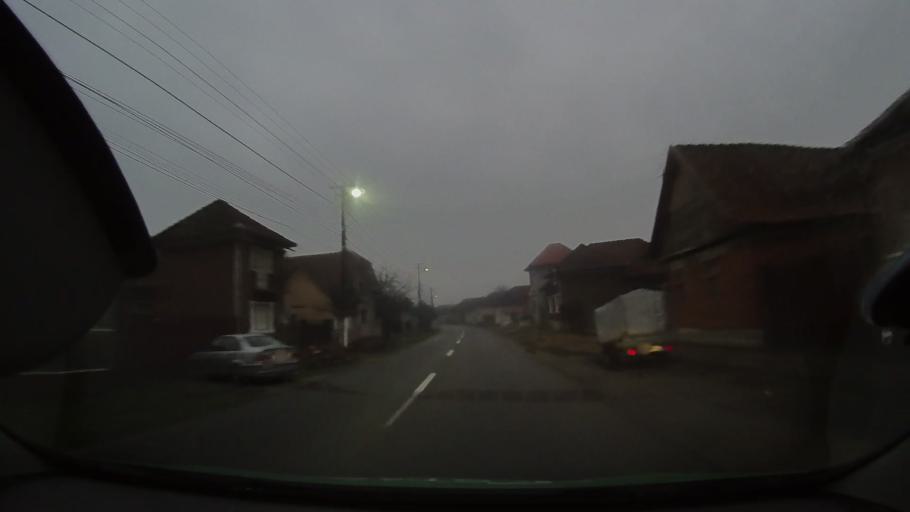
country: RO
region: Arad
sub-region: Comuna Beliu
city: Beliu
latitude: 46.4890
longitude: 21.9888
